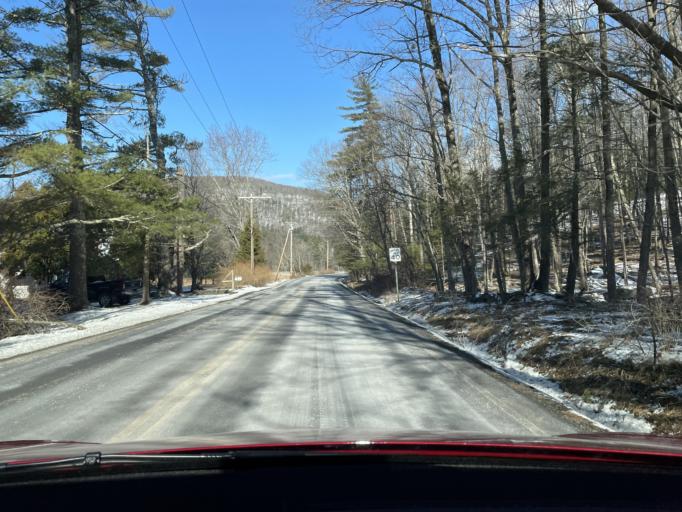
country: US
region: New York
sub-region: Ulster County
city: Woodstock
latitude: 42.0529
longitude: -74.1544
